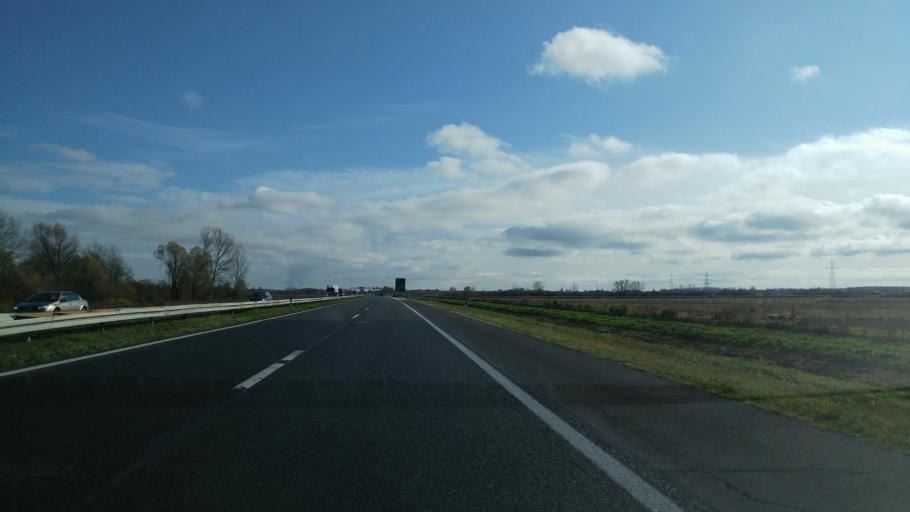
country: HR
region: Grad Zagreb
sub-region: Sesvete
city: Sesvete
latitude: 45.7728
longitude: 16.2065
